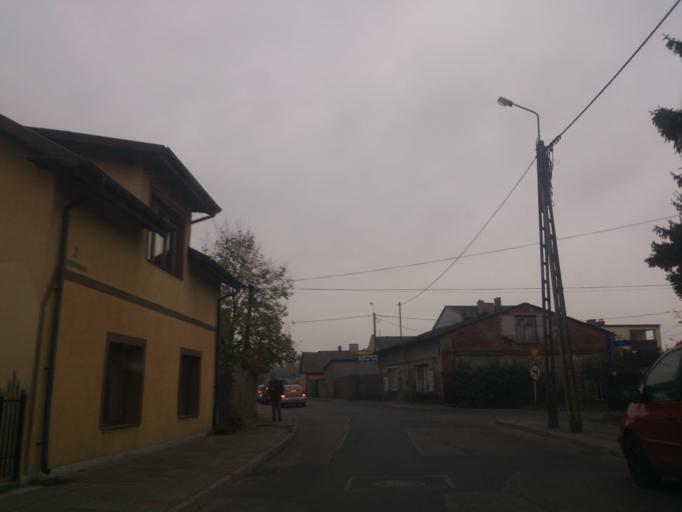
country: PL
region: Kujawsko-Pomorskie
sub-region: Powiat golubsko-dobrzynski
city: Golub-Dobrzyn
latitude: 53.1072
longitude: 19.0573
